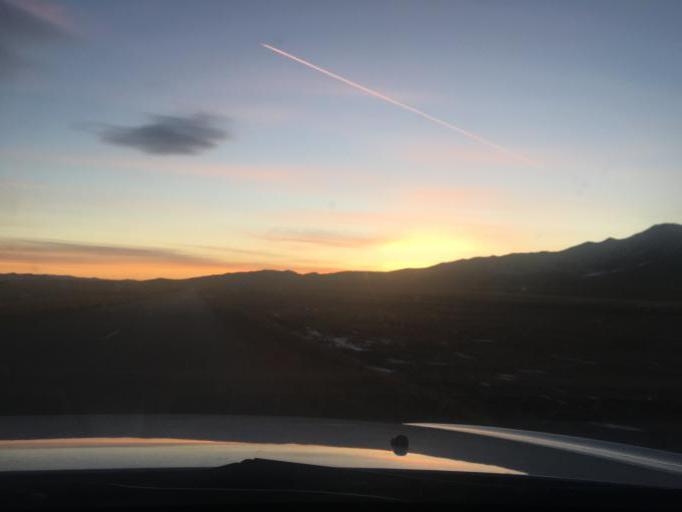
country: MN
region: Central Aimak
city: Mandal
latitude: 48.0889
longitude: 106.5988
